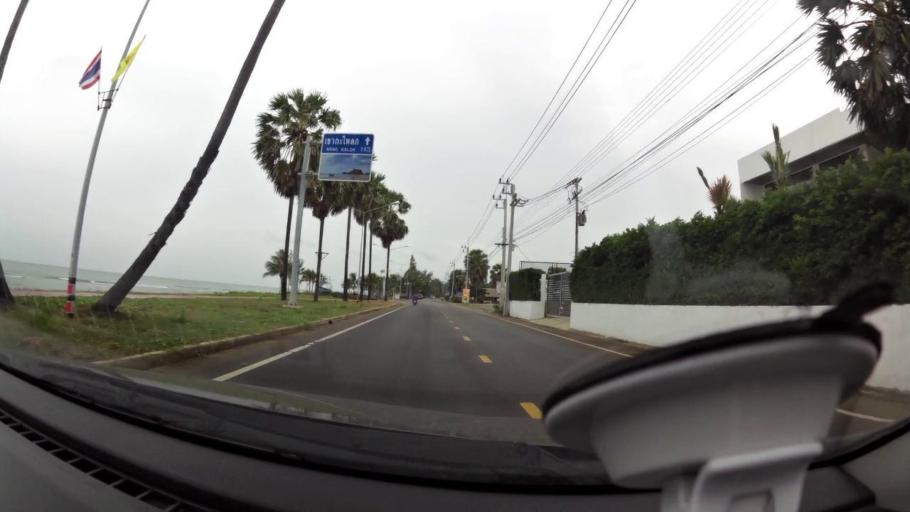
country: TH
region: Prachuap Khiri Khan
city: Pran Buri
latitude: 12.3722
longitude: 100.0000
